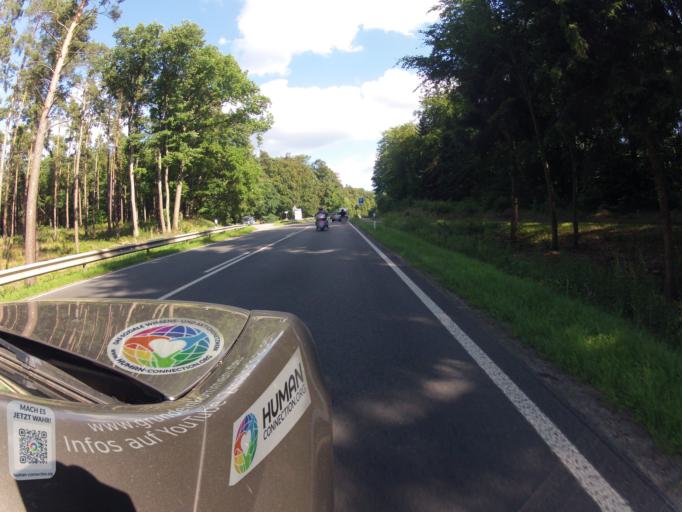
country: DE
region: Mecklenburg-Vorpommern
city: Seebad Bansin
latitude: 53.9727
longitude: 14.1156
